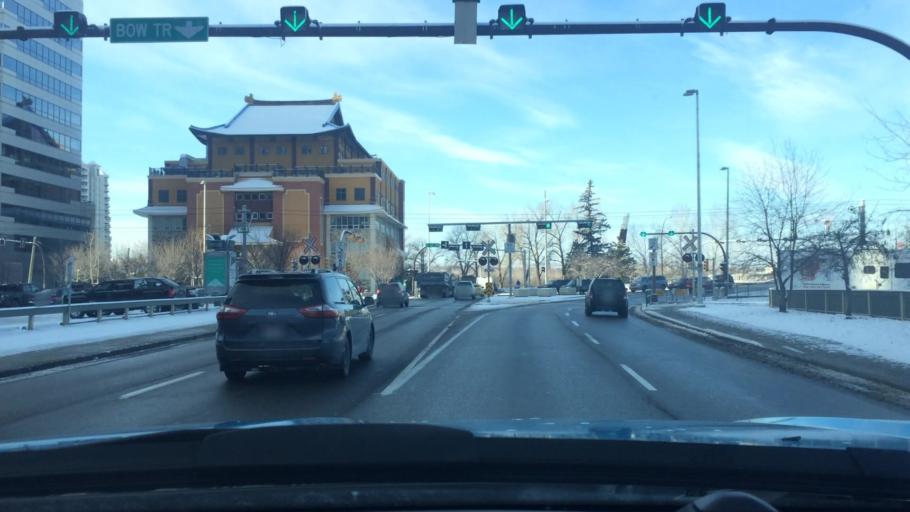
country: CA
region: Alberta
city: Calgary
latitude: 51.0499
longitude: -114.0823
